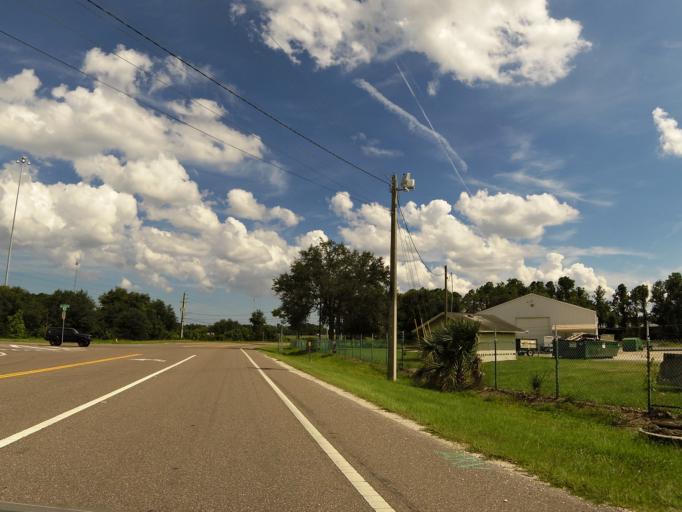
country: US
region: Florida
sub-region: Duval County
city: Jacksonville
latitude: 30.4171
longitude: -81.5669
